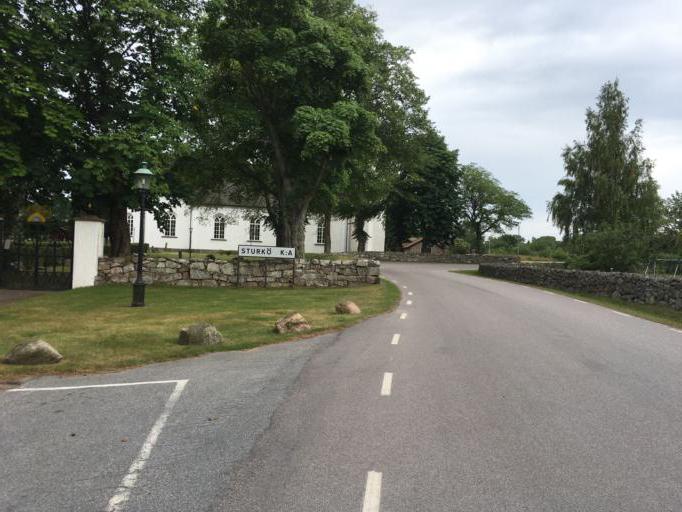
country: SE
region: Blekinge
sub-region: Karlskrona Kommun
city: Sturko
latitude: 56.0892
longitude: 15.6957
